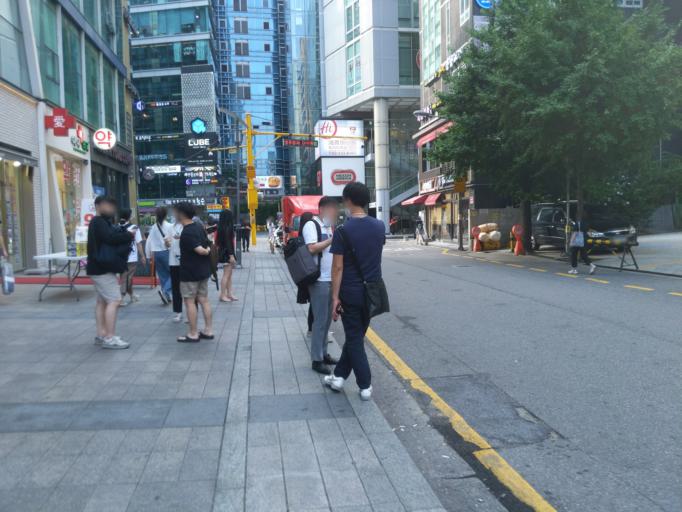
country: KR
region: Seoul
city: Seoul
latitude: 37.5020
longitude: 127.0249
